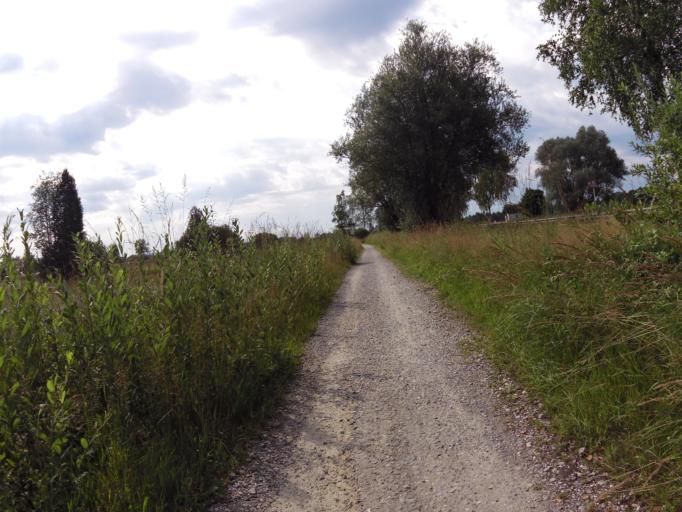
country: DE
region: Bavaria
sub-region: Upper Bavaria
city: Diessen am Ammersee
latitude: 47.9361
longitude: 11.1084
